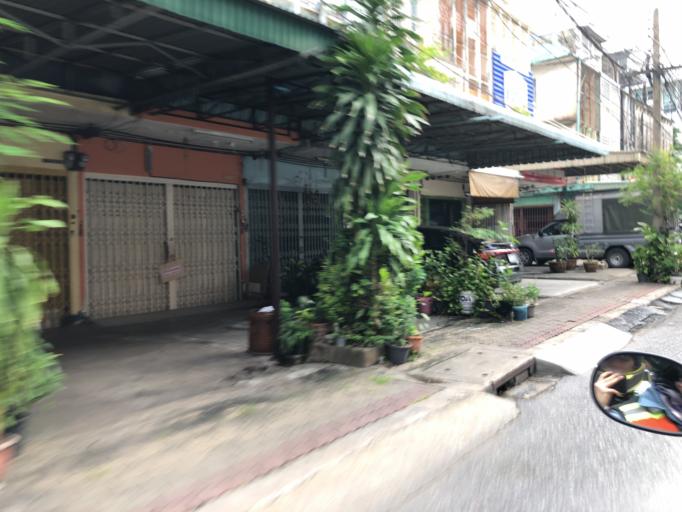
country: TH
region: Bangkok
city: Yan Nawa
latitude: 13.7047
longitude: 100.5396
